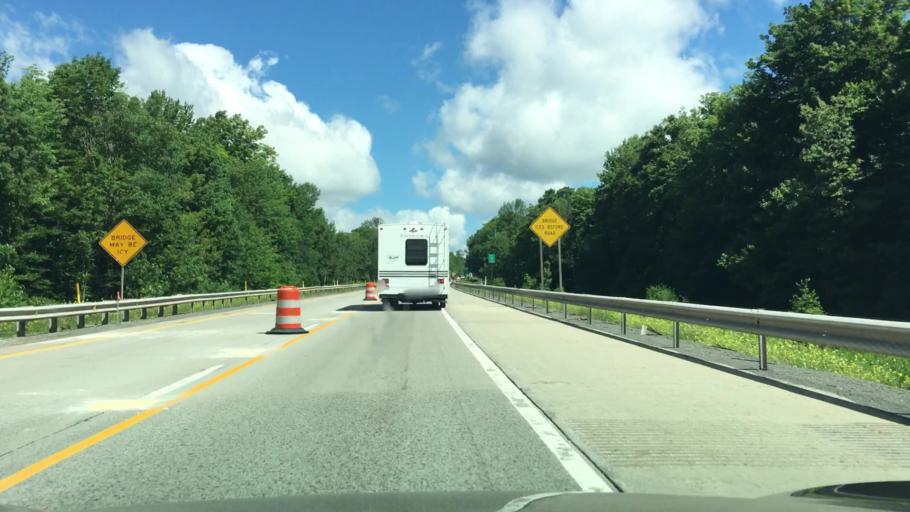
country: US
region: Pennsylvania
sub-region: Lackawanna County
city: Moscow
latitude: 41.2455
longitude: -75.5140
